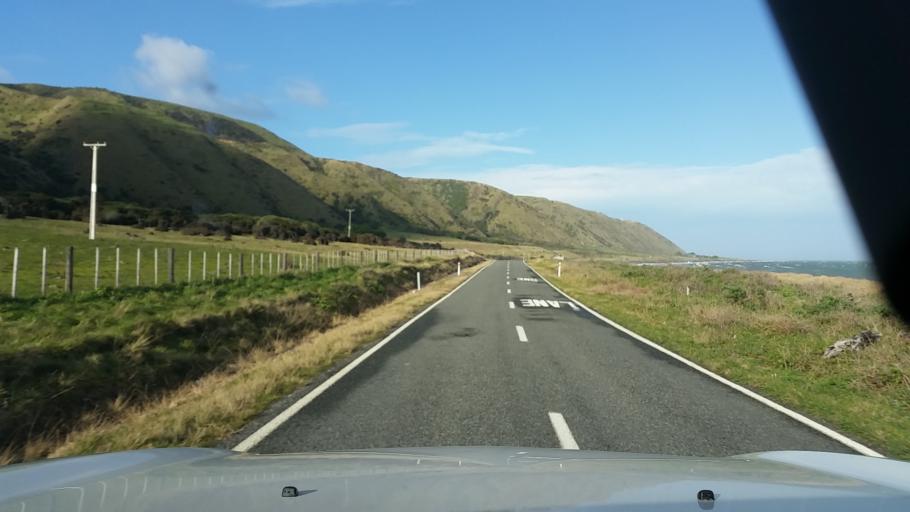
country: NZ
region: Wellington
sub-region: South Wairarapa District
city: Waipawa
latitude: -41.4966
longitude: 175.2092
